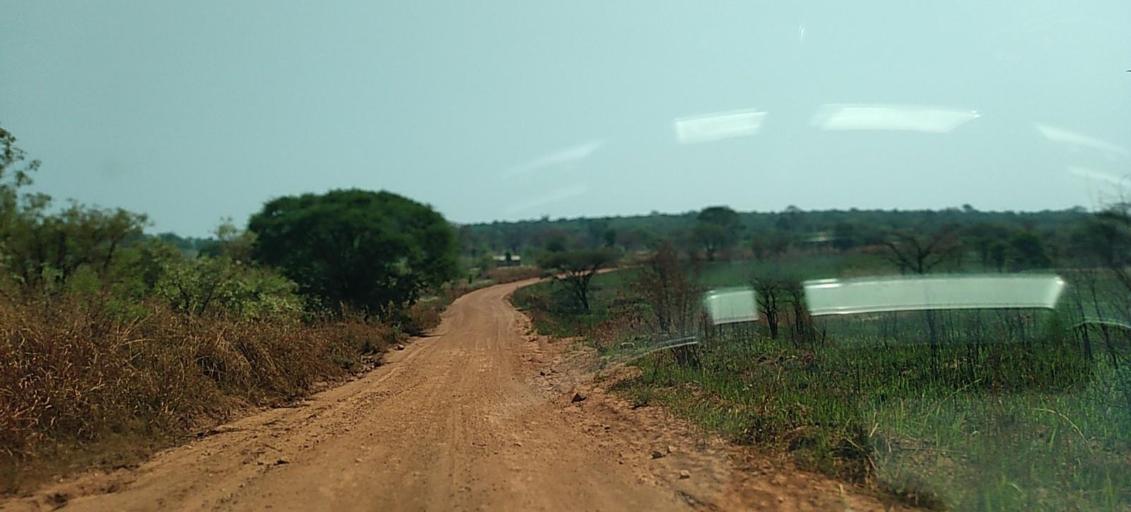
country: ZM
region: North-Western
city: Kansanshi
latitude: -12.0049
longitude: 26.5556
